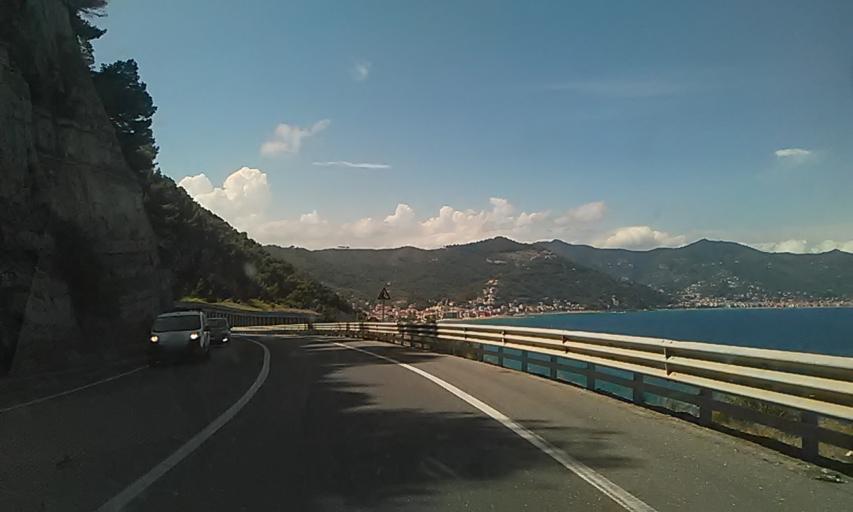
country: IT
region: Liguria
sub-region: Provincia di Savona
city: Marina di Andora
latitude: 43.9614
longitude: 8.1690
